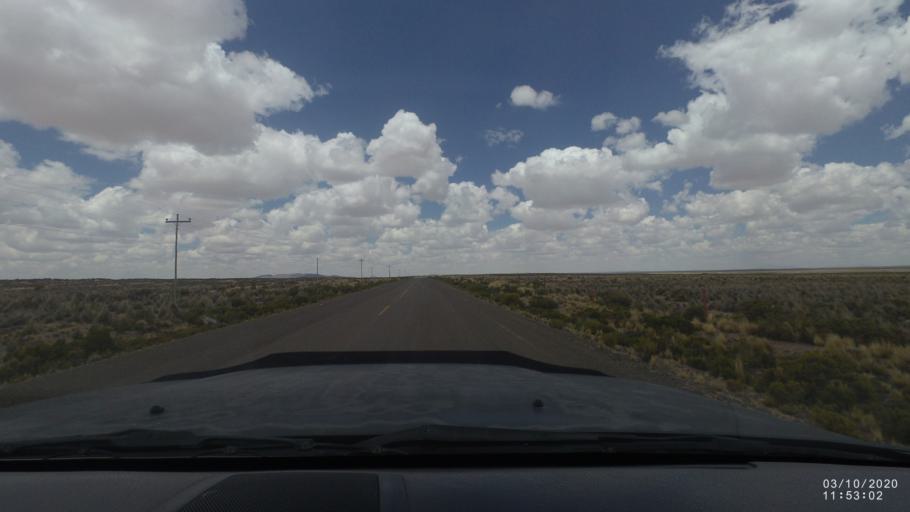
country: BO
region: Oruro
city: Poopo
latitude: -18.4706
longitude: -67.6022
